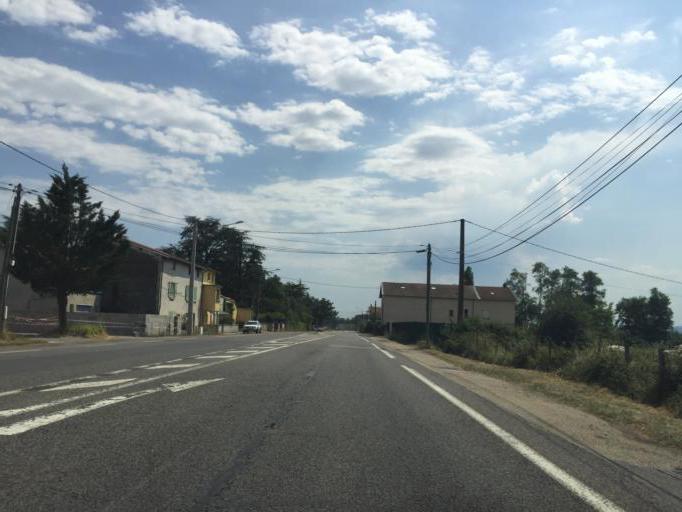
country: FR
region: Rhone-Alpes
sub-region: Departement du Rhone
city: Charbonnieres-les-Bains
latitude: 45.7973
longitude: 4.7411
